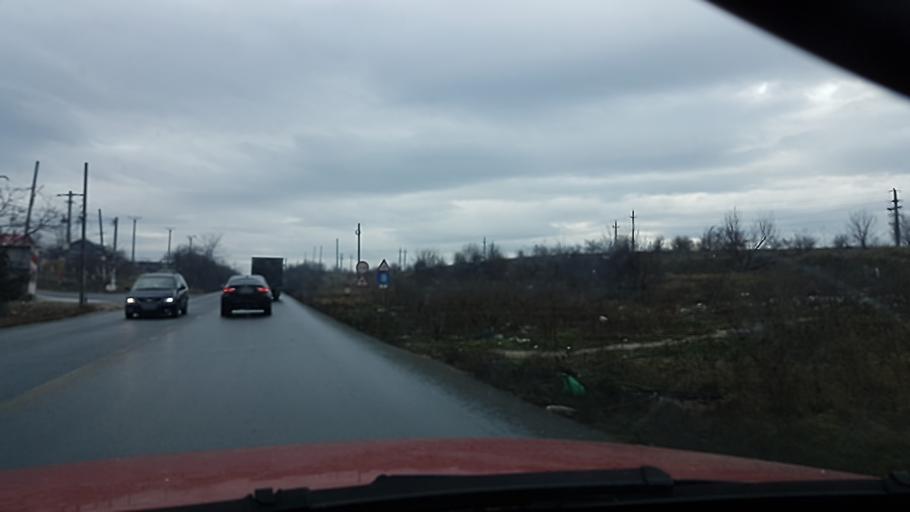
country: RO
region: Ilfov
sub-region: Comuna Glina
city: Catelu
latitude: 44.3886
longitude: 26.2259
